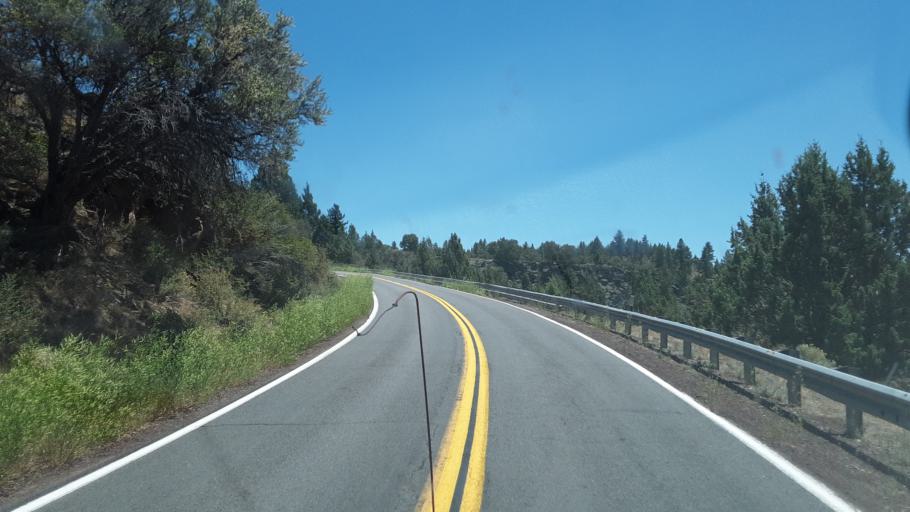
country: US
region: California
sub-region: Lassen County
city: Susanville
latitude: 40.6413
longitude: -120.6574
